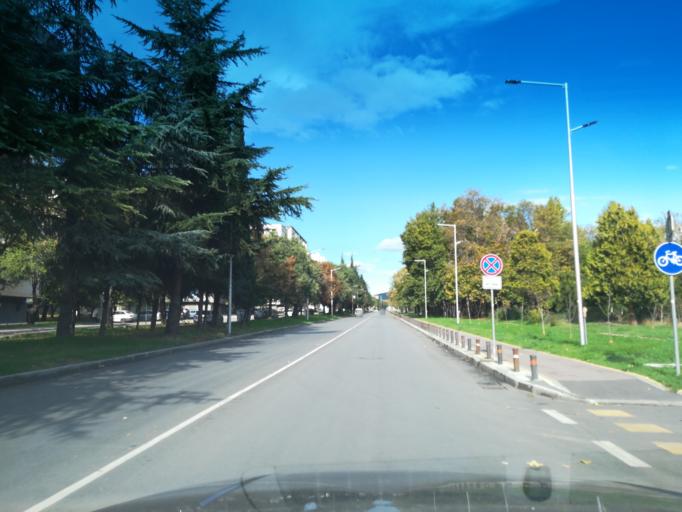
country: BG
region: Stara Zagora
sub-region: Obshtina Stara Zagora
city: Stara Zagora
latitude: 42.4345
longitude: 25.6369
